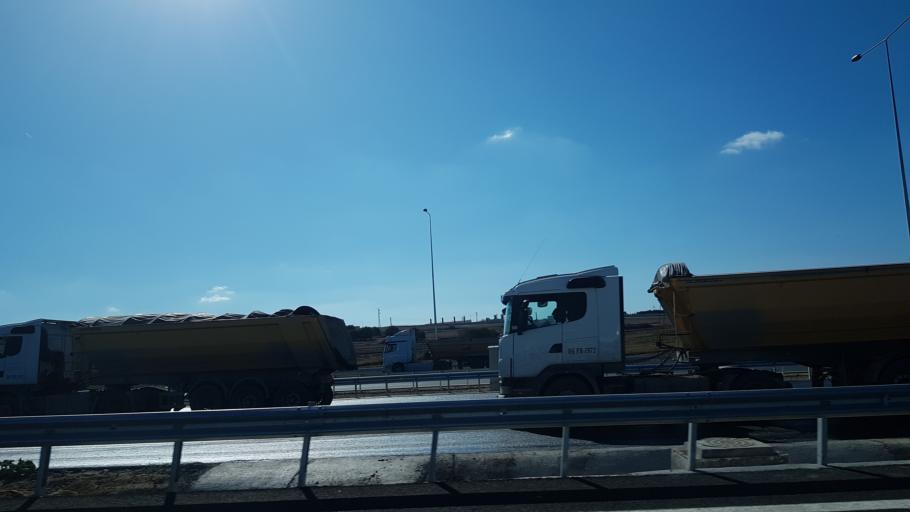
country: TR
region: Istanbul
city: Silivri
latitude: 41.1153
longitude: 28.1747
